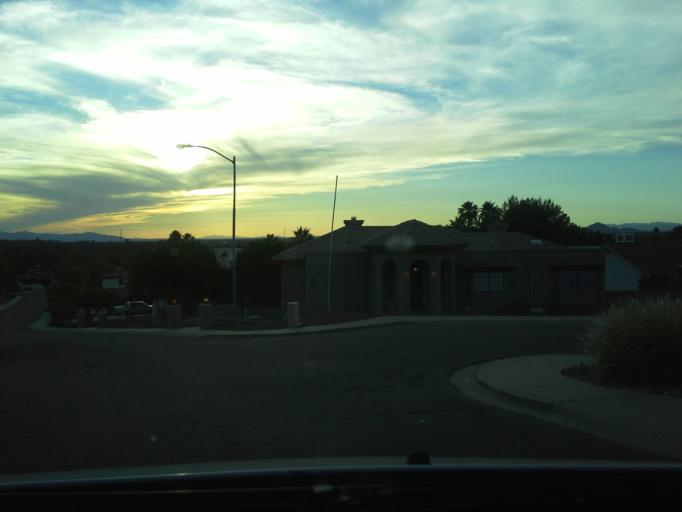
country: US
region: Arizona
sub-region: Maricopa County
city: Paradise Valley
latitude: 33.6236
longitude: -112.0591
